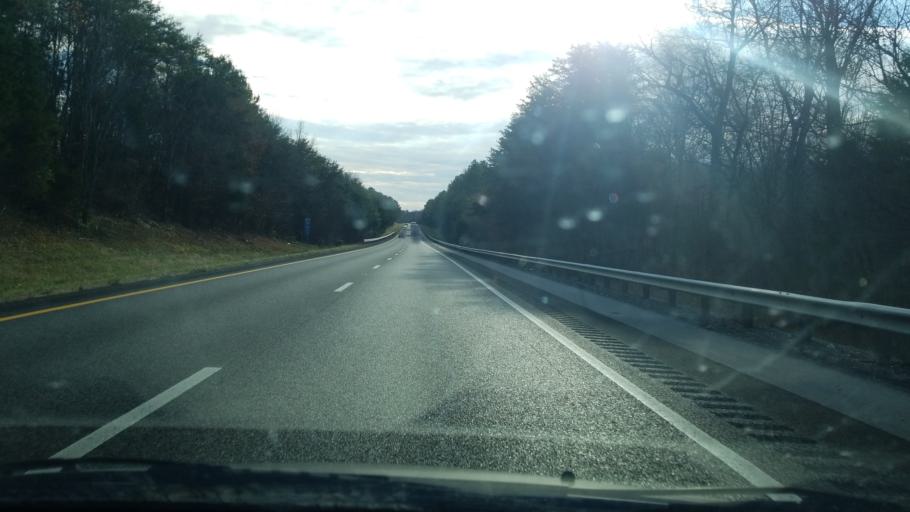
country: US
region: Tennessee
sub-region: Meigs County
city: Decatur
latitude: 35.3853
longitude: -84.7274
